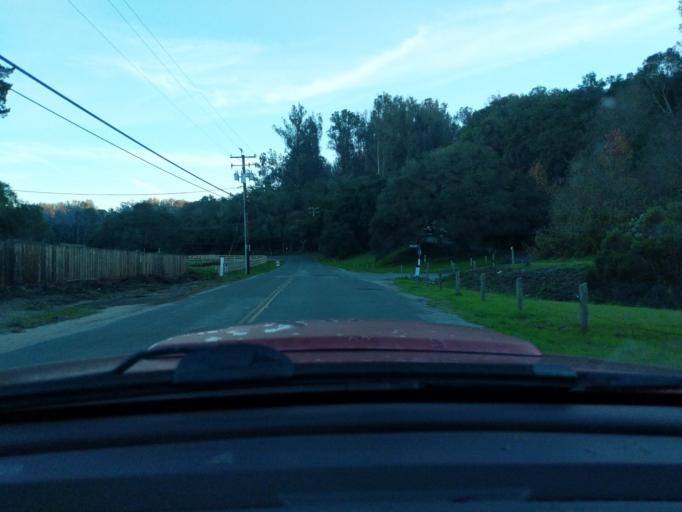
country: US
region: California
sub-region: San Benito County
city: Aromas
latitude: 36.8398
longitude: -121.6734
